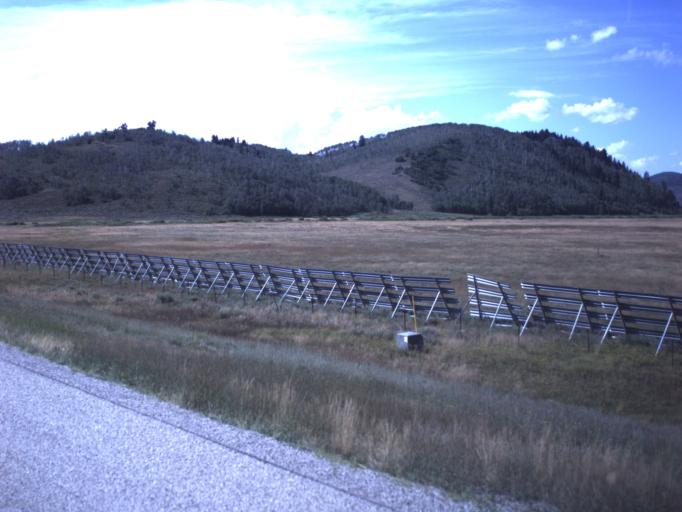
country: US
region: Utah
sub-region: Wasatch County
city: Heber
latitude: 40.2797
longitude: -111.2219
